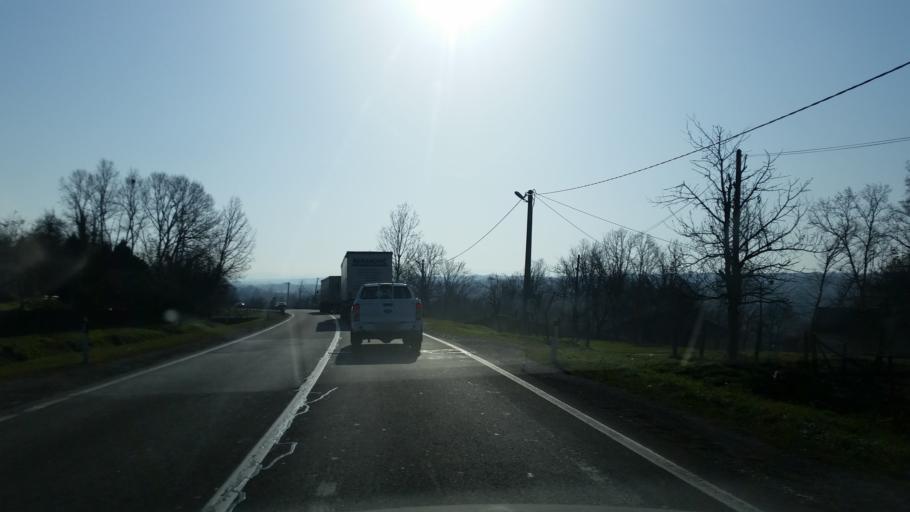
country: RS
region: Central Serbia
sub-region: Kolubarski Okrug
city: Lajkovac
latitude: 44.3502
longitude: 20.1925
